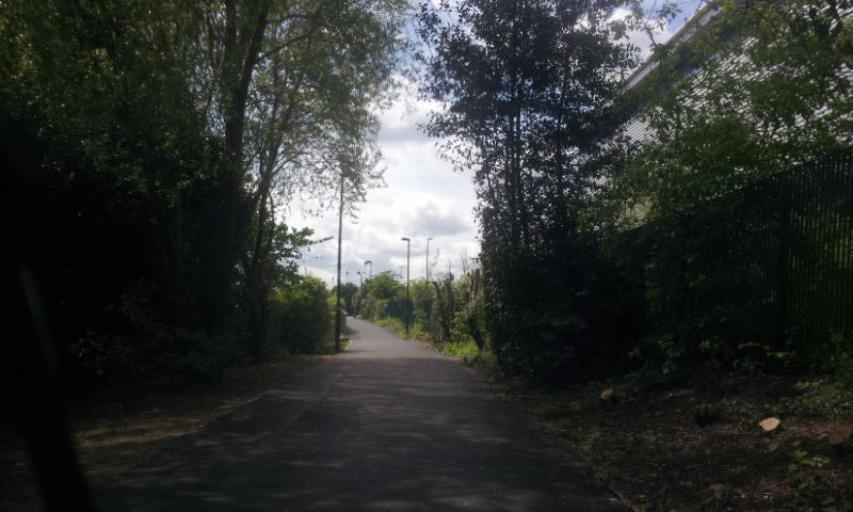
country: GB
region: England
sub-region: Greater London
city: Catford
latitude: 51.4315
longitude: -0.0307
